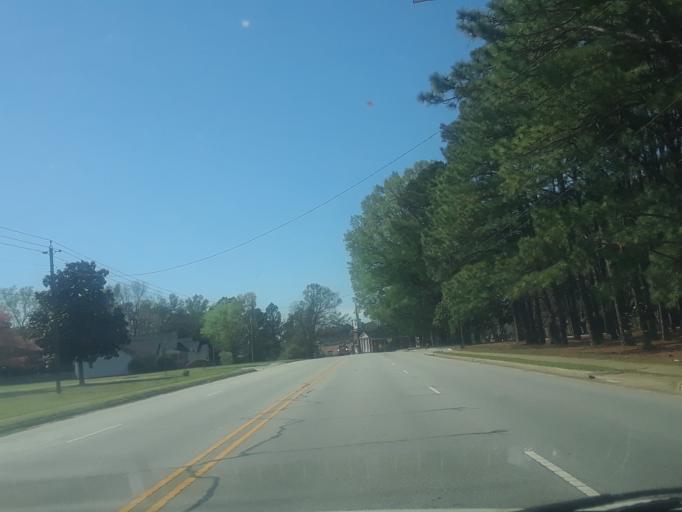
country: US
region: North Carolina
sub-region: Harnett County
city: Erwin
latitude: 35.3253
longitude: -78.6637
